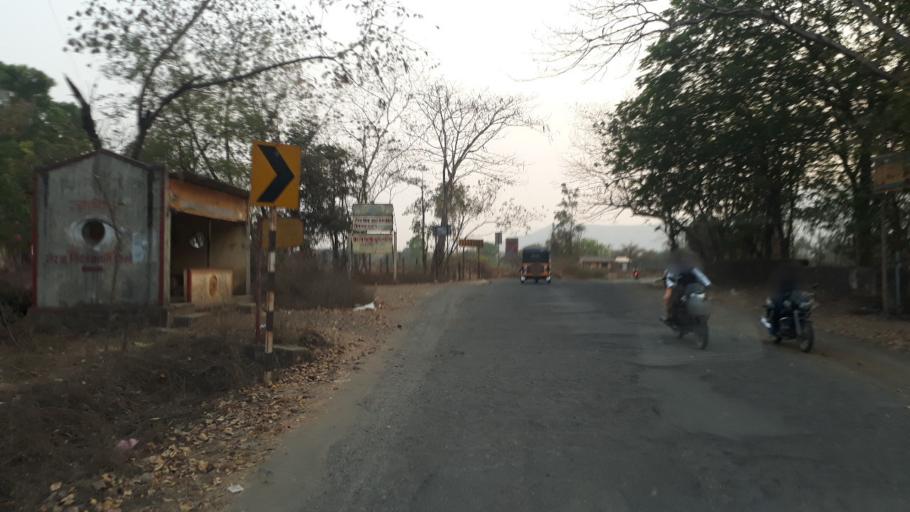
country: IN
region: Maharashtra
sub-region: Raigarh
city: Neral
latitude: 19.0411
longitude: 73.3309
